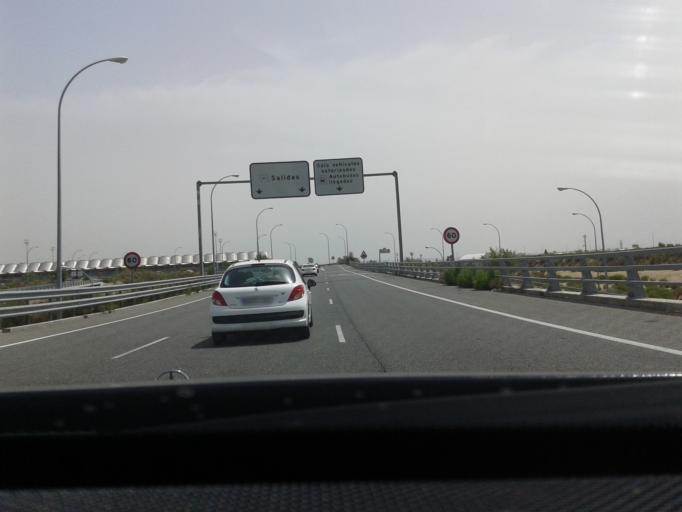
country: ES
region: Madrid
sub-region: Provincia de Madrid
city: Barajas de Madrid
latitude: 40.4865
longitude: -3.5977
